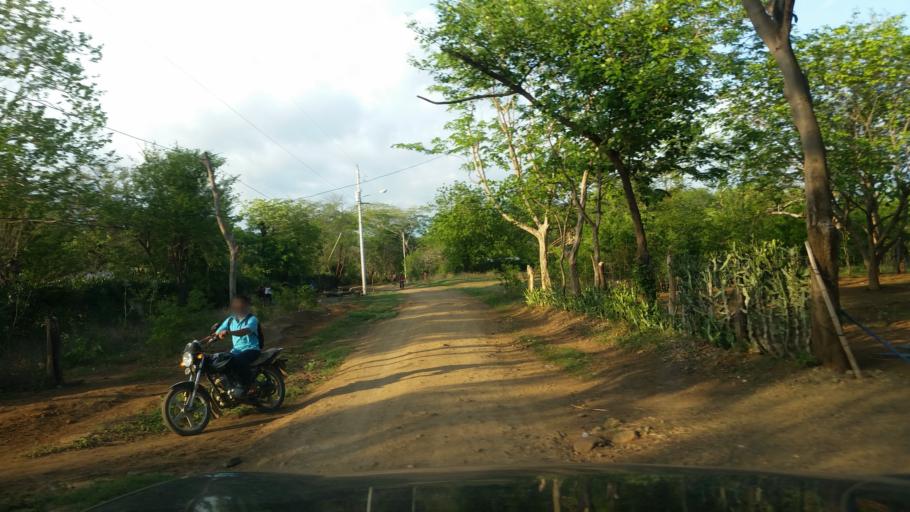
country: NI
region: Managua
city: Masachapa
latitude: 11.7802
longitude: -86.4747
